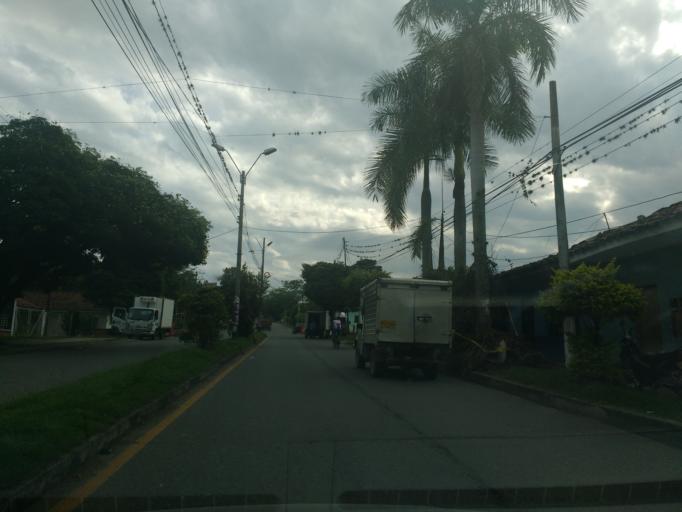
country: CO
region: Cauca
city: Miranda
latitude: 3.2594
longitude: -76.2276
